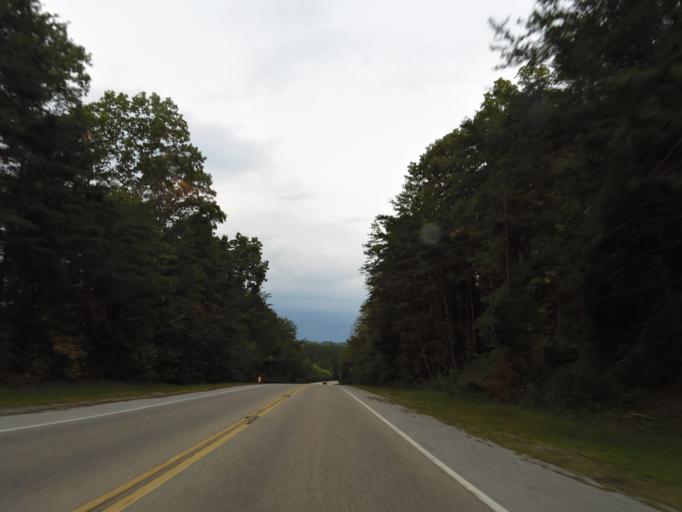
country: US
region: Tennessee
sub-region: Loudon County
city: Loudon
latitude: 35.6865
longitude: -84.2631
